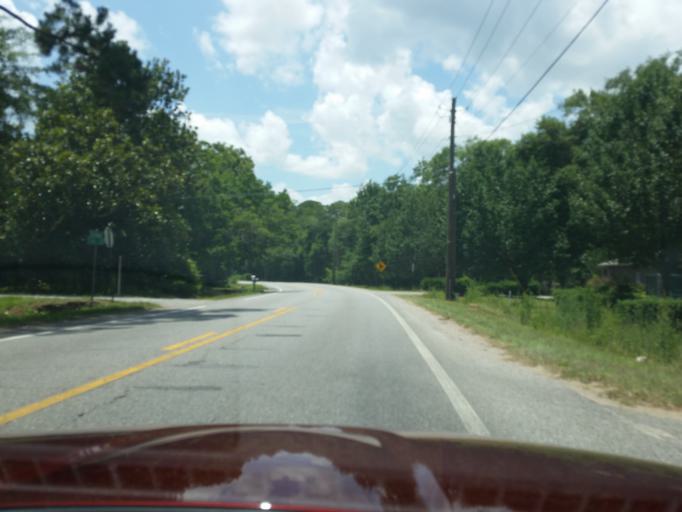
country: US
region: Florida
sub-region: Escambia County
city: Gonzalez
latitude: 30.5822
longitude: -87.2891
